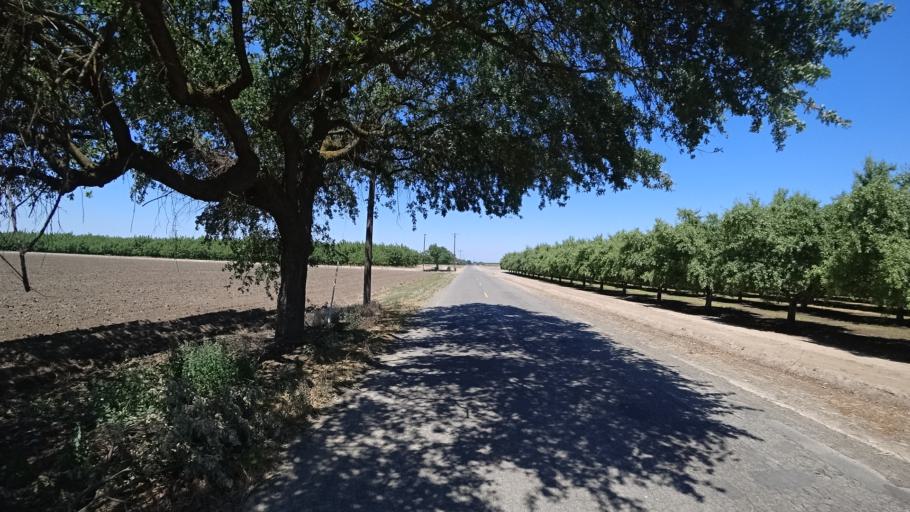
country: US
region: California
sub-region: Kings County
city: Lucerne
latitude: 36.4112
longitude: -119.6010
